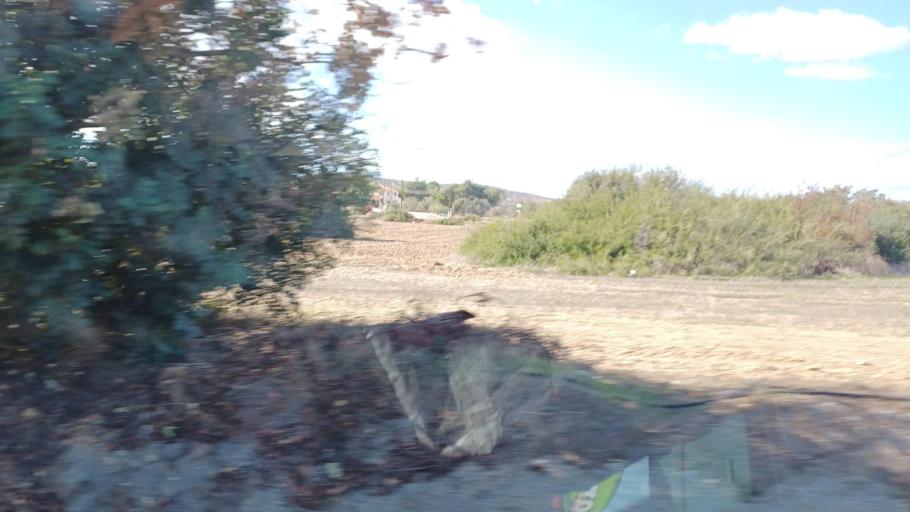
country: CY
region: Limassol
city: Pyrgos
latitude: 34.7285
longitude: 33.2049
